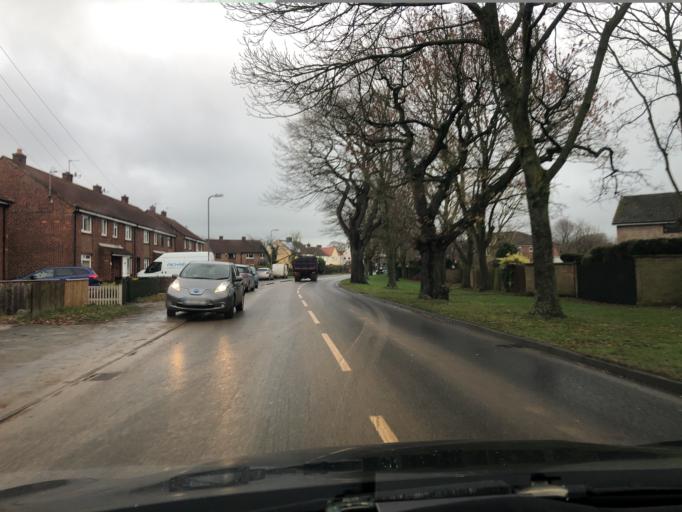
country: GB
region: England
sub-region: North Yorkshire
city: Stokesley
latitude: 54.4674
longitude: -1.2024
